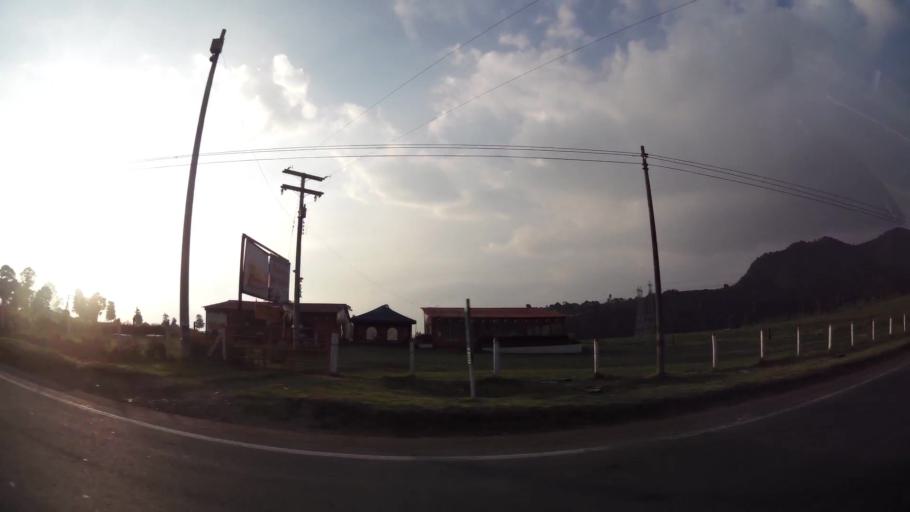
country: CO
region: Cundinamarca
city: Cota
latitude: 4.7732
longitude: -74.1456
